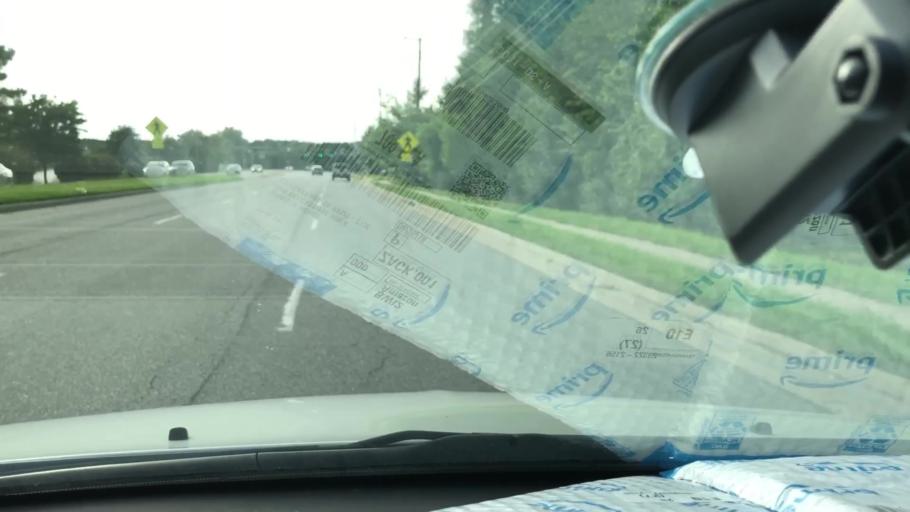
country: US
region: Virginia
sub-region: City of Chesapeake
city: Chesapeake
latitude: 36.7113
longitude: -76.2740
